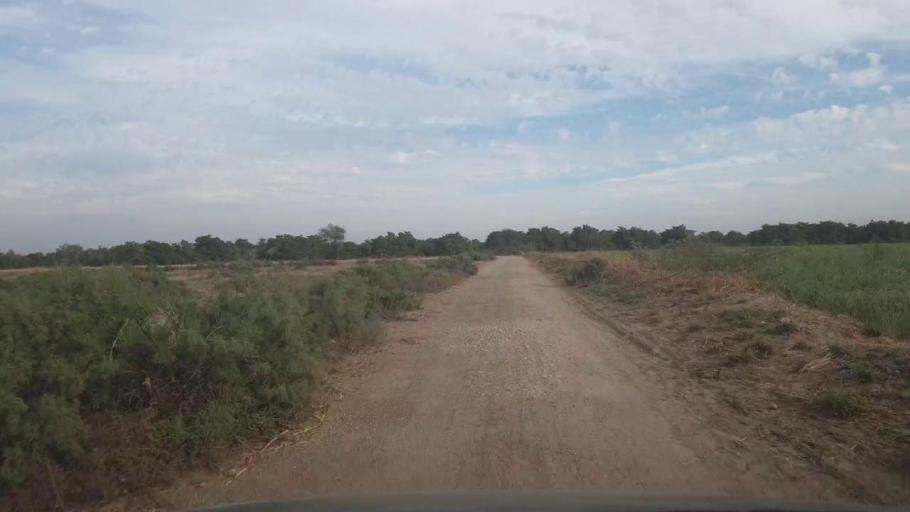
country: PK
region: Sindh
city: Samaro
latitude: 25.3278
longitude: 69.2656
